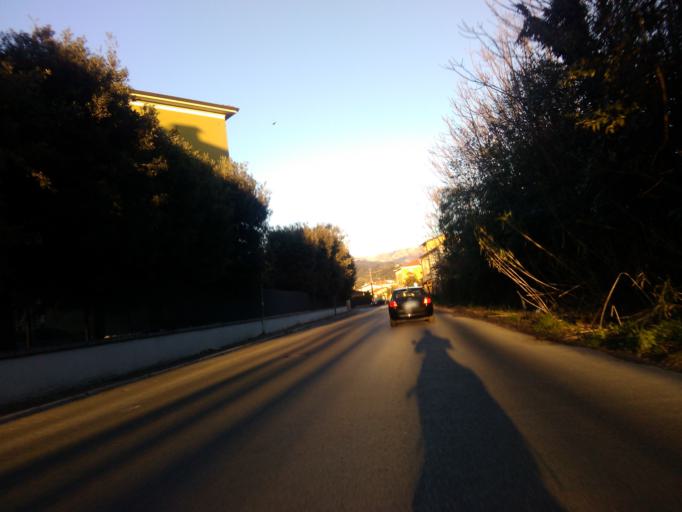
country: IT
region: Tuscany
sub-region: Provincia di Massa-Carrara
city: Carrara
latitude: 44.0469
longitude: 10.0546
